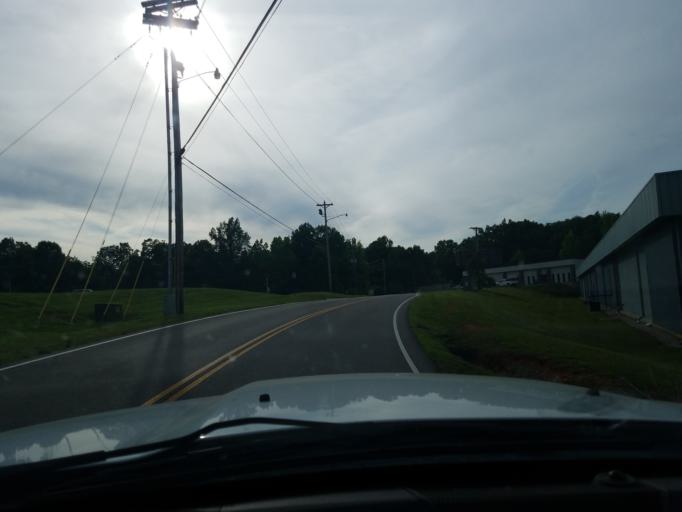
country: US
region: Tennessee
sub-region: Putnam County
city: Cookeville
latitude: 36.1345
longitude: -85.5414
